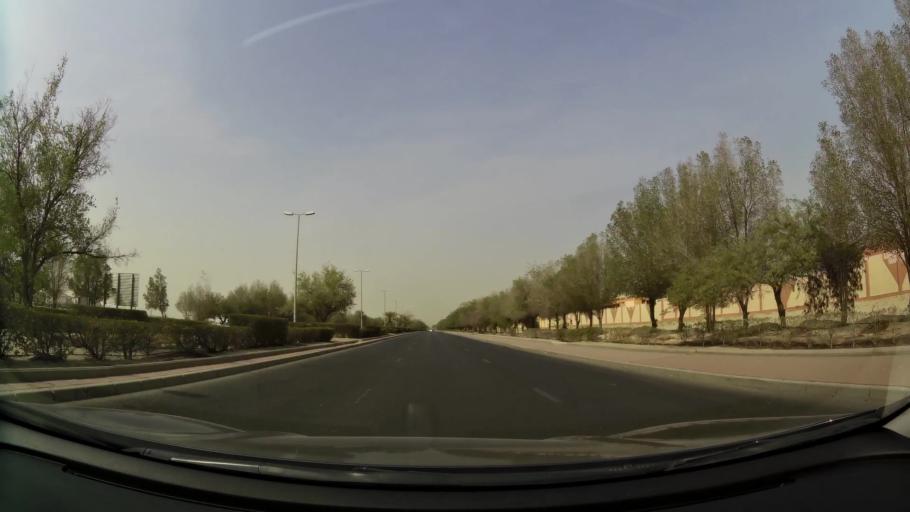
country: KW
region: Al Farwaniyah
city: Al Farwaniyah
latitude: 29.2473
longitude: 47.9298
